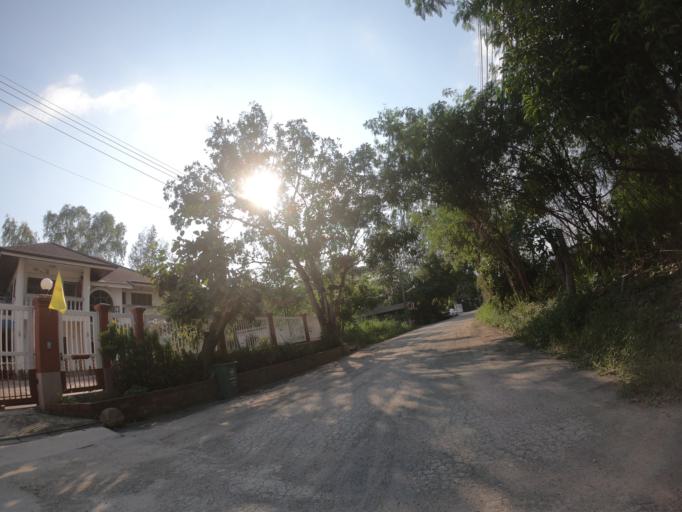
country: TH
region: Chiang Mai
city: San Sai
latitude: 18.8313
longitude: 99.0077
